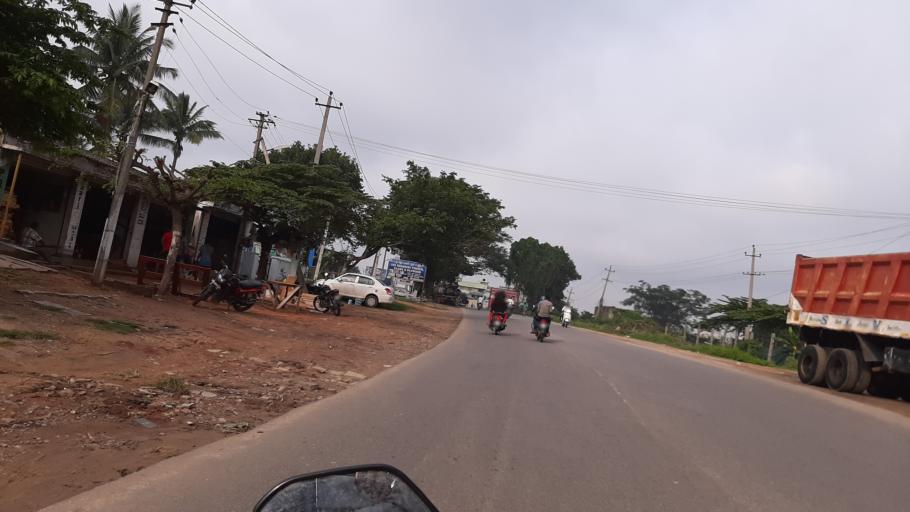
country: IN
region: Karnataka
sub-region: Bangalore Rural
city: Nelamangala
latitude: 12.9700
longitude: 77.4097
